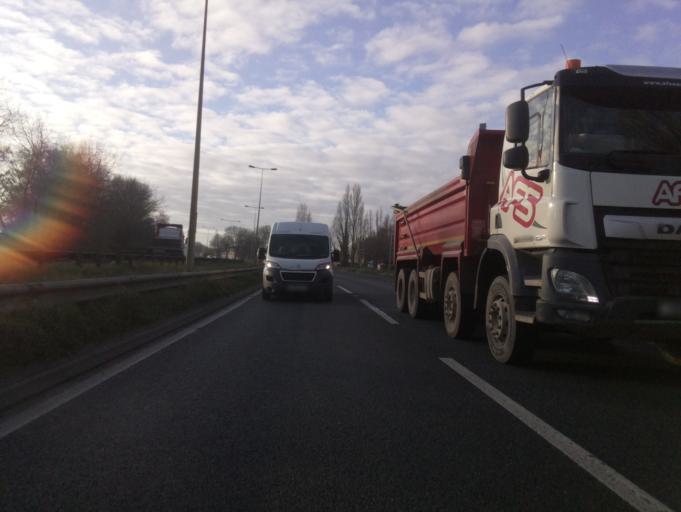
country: GB
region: England
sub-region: Staffordshire
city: Burton upon Trent
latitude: 52.7814
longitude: -1.6811
